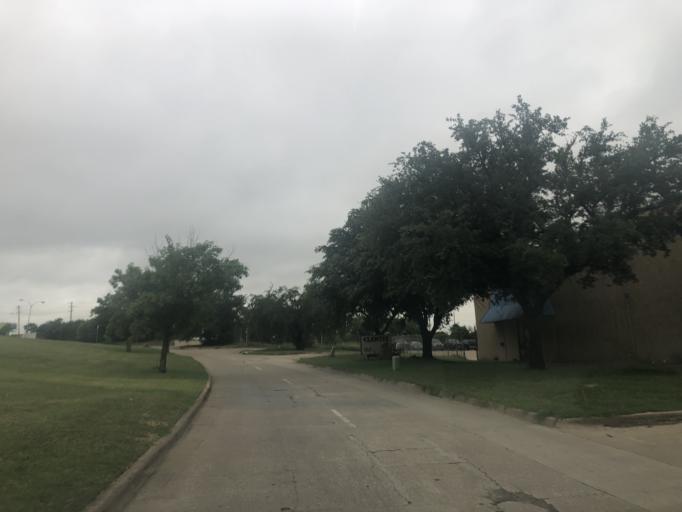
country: US
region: Texas
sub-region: Dallas County
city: Cockrell Hill
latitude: 32.7745
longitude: -96.8642
